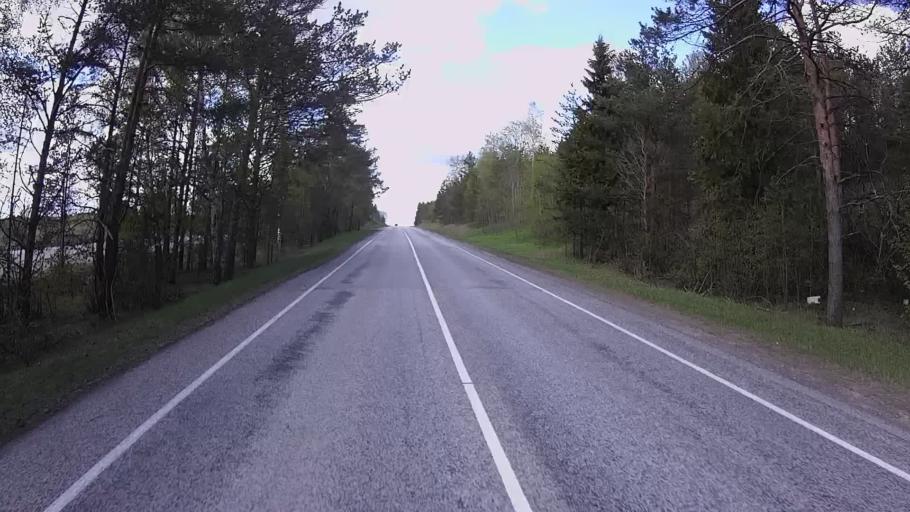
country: EE
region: Jogevamaa
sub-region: Jogeva linn
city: Jogeva
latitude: 58.7814
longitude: 26.4745
